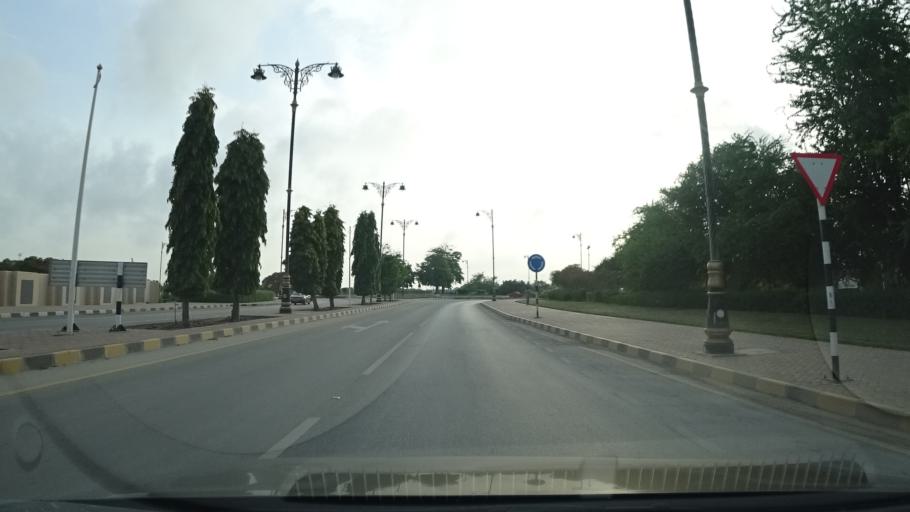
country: OM
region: Zufar
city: Salalah
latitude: 17.0262
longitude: 54.1446
